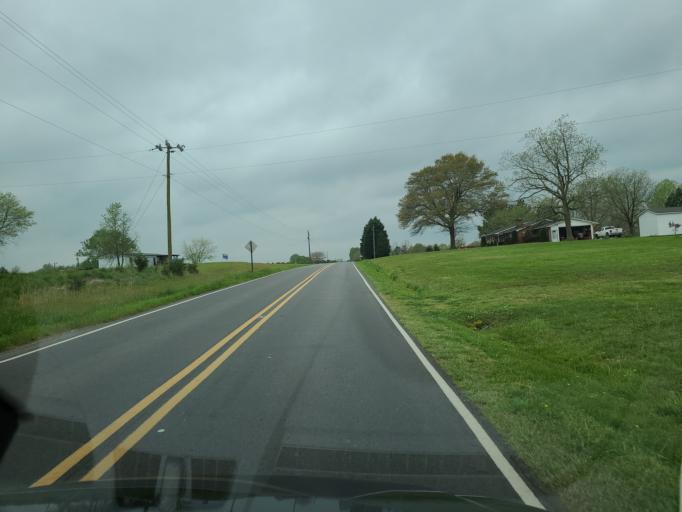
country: US
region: North Carolina
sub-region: Gaston County
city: Cherryville
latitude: 35.4274
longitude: -81.4345
